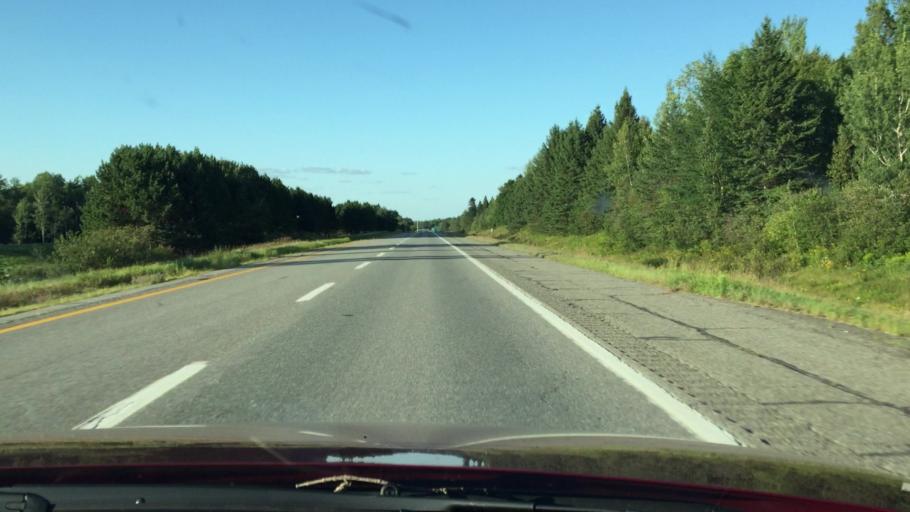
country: US
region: Maine
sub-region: Penobscot County
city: Patten
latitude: 45.8596
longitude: -68.4211
